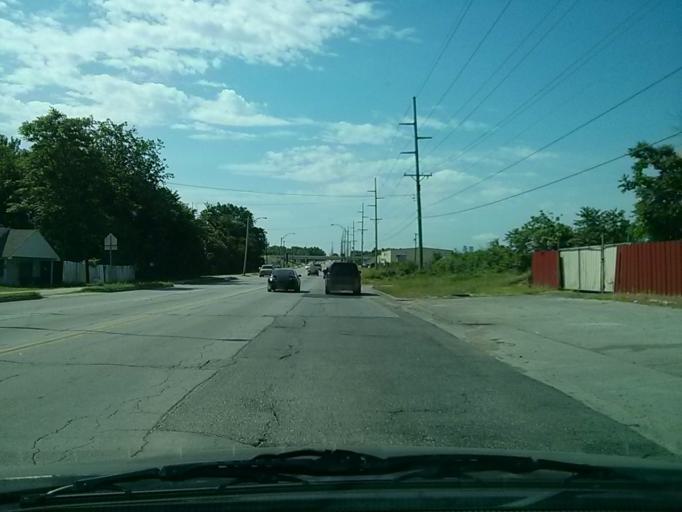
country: US
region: Oklahoma
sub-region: Tulsa County
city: Turley
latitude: 36.2021
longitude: -95.9757
